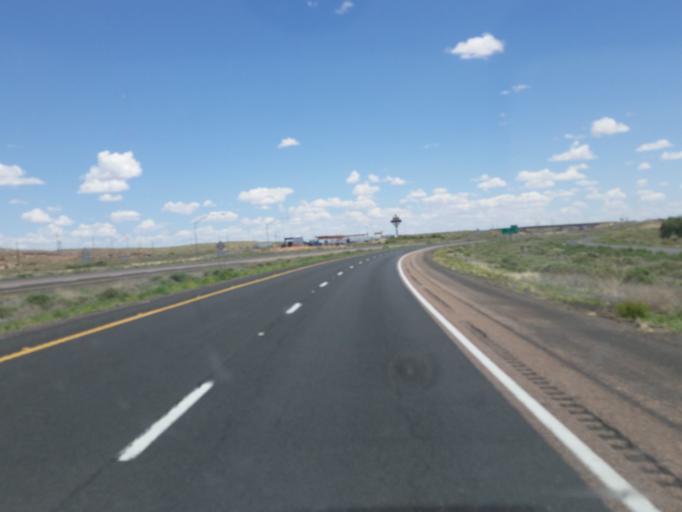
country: US
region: Arizona
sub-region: Navajo County
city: Joseph City
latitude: 34.9553
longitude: -110.3193
